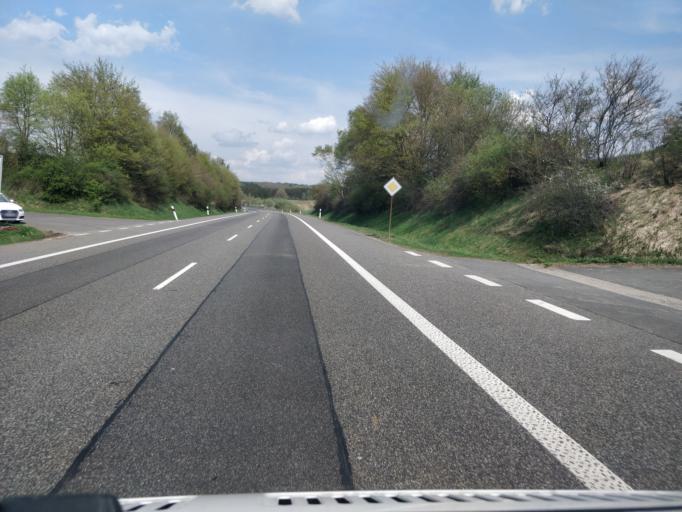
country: DE
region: North Rhine-Westphalia
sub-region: Regierungsbezirk Koln
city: Dahlem
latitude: 50.3962
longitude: 6.5520
